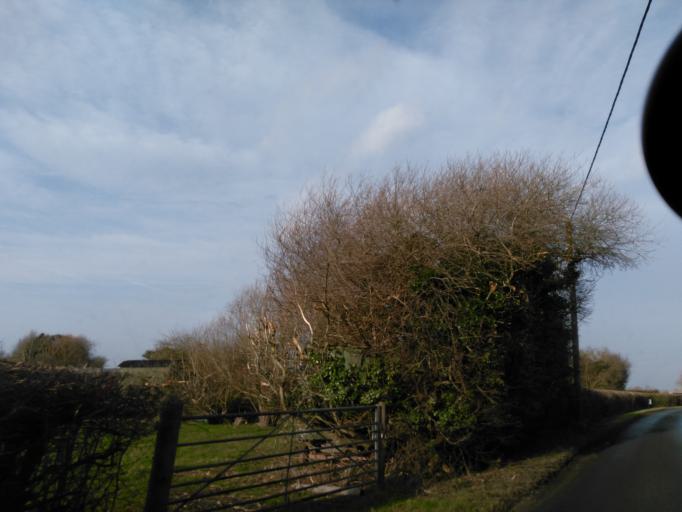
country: GB
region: England
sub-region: Wiltshire
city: Marston
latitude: 51.3197
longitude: -2.0513
